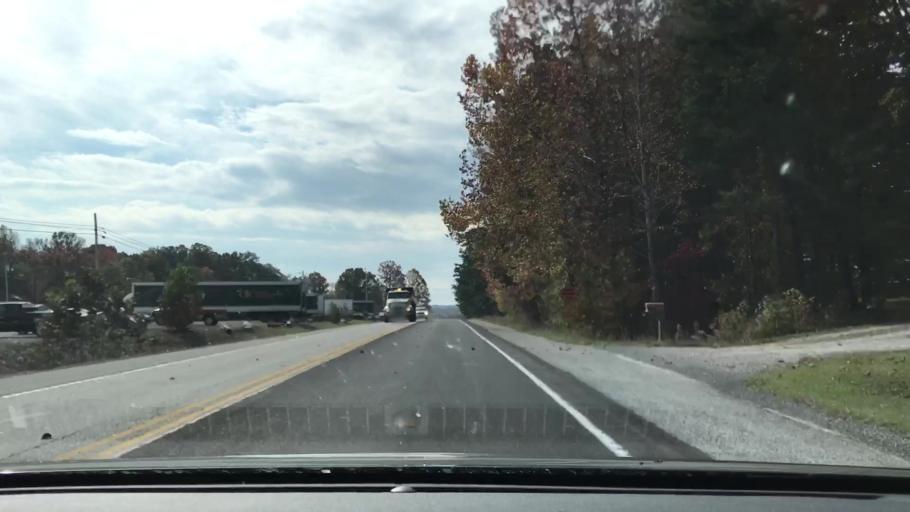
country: US
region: Kentucky
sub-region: McCreary County
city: Pine Knot
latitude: 36.5759
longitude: -84.4424
